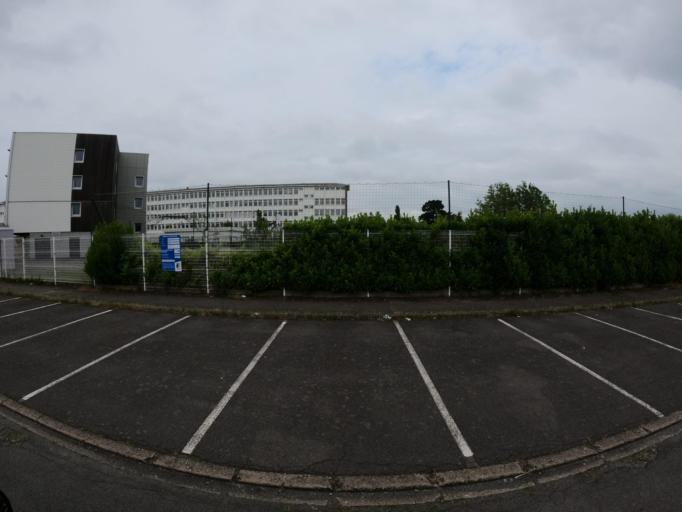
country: FR
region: Pays de la Loire
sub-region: Departement de la Loire-Atlantique
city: Saint-Nazaire
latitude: 47.2751
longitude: -2.2304
